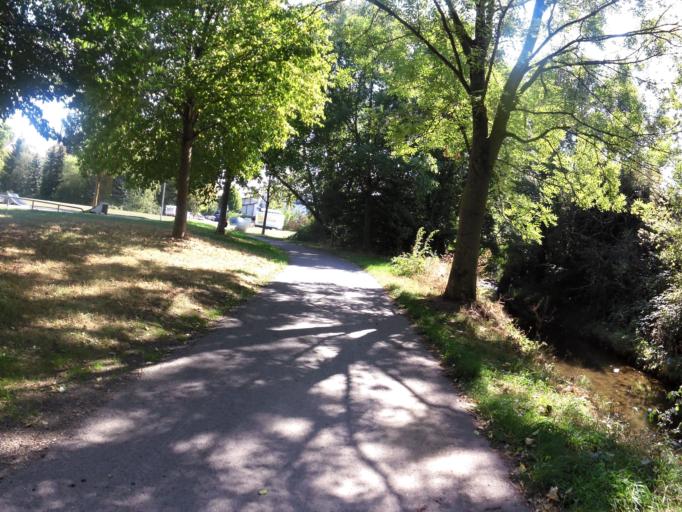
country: DE
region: North Rhine-Westphalia
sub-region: Regierungsbezirk Koln
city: Wurselen
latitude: 50.7964
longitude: 6.1213
